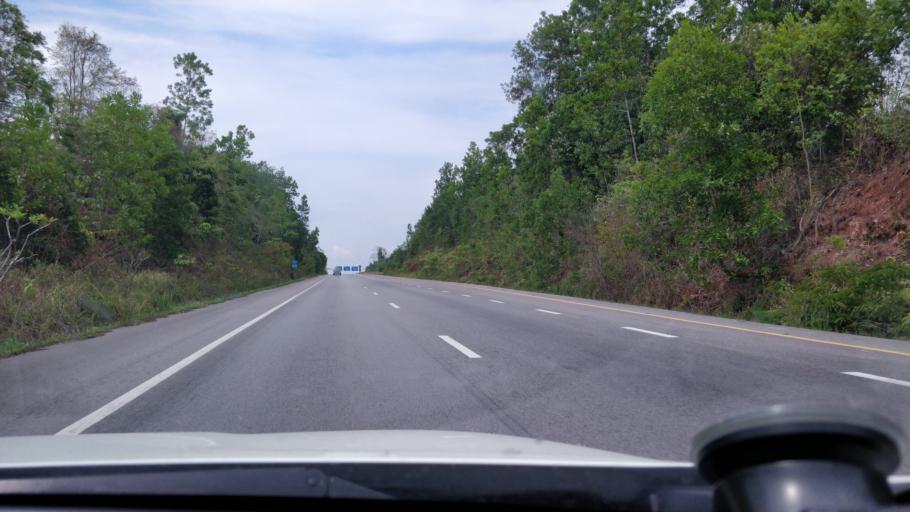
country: TH
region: Surat Thani
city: Khian Sa
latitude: 8.8113
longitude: 99.1660
